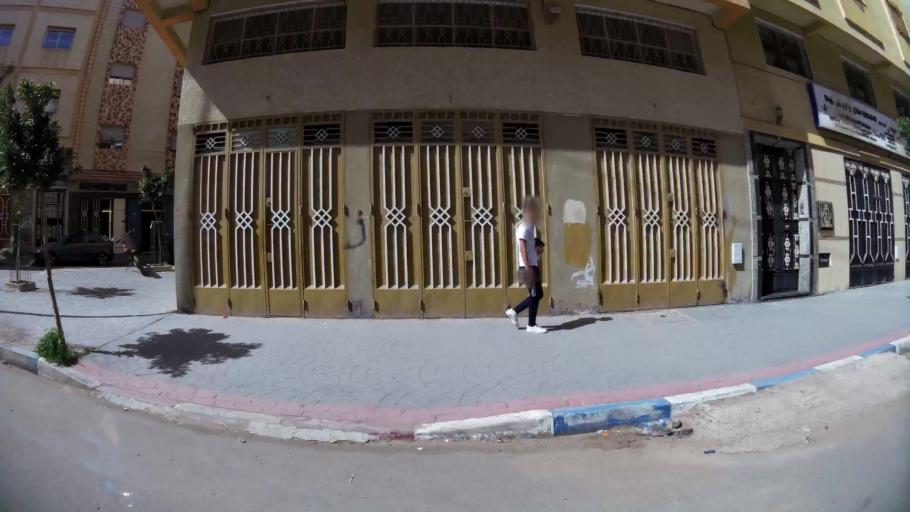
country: MA
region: Tanger-Tetouan
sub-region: Tanger-Assilah
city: Tangier
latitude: 35.7342
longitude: -5.8033
